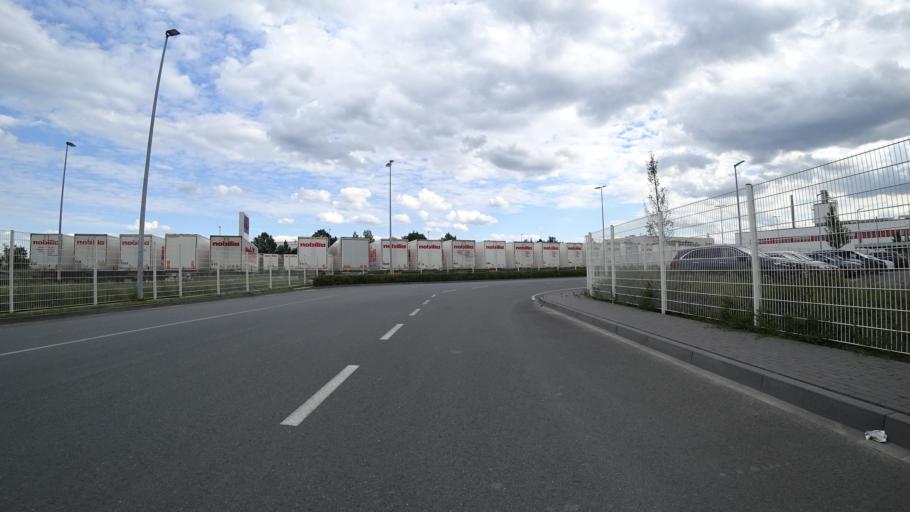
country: DE
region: North Rhine-Westphalia
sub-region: Regierungsbezirk Detmold
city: Guetersloh
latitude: 51.8914
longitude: 8.4450
